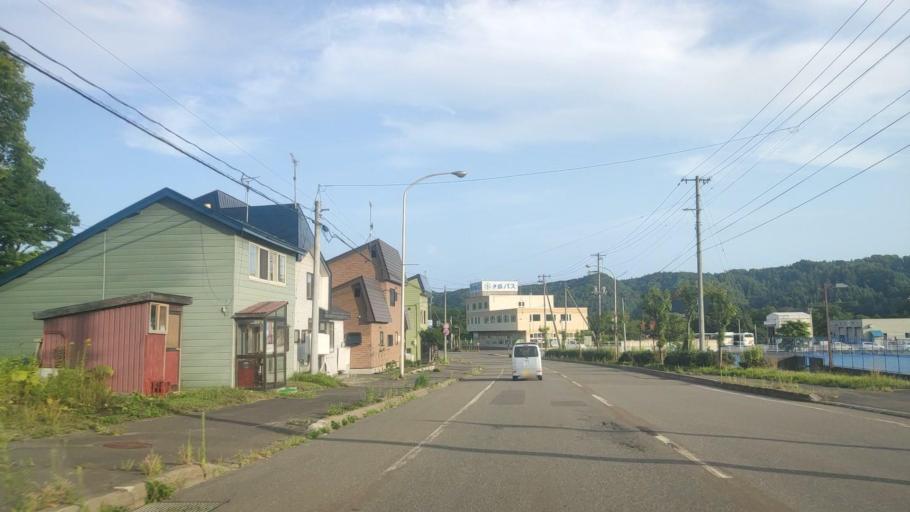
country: JP
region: Hokkaido
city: Iwamizawa
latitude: 43.0299
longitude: 141.9676
